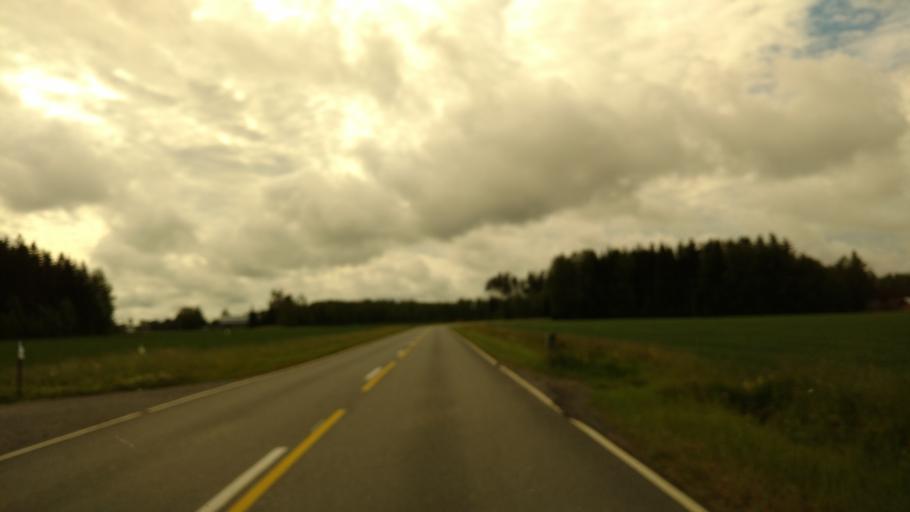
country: FI
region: Varsinais-Suomi
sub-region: Loimaa
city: Koski Tl
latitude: 60.5894
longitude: 23.1328
